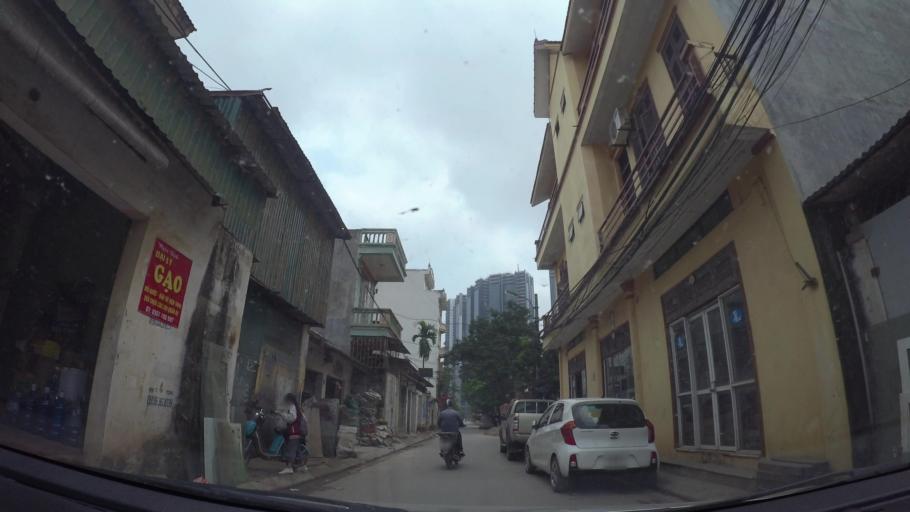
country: VN
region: Ha Noi
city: Tay Ho
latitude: 21.0893
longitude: 105.7919
